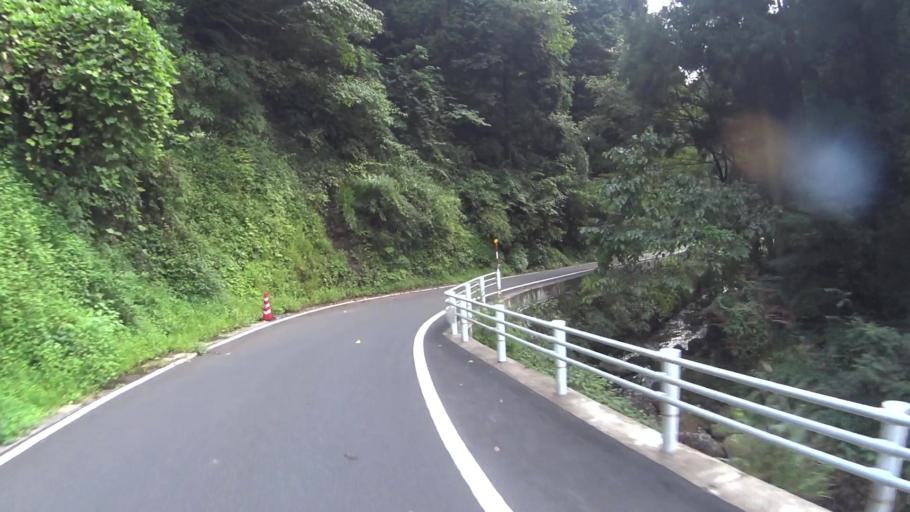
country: JP
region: Kyoto
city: Miyazu
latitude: 35.6114
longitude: 135.2079
